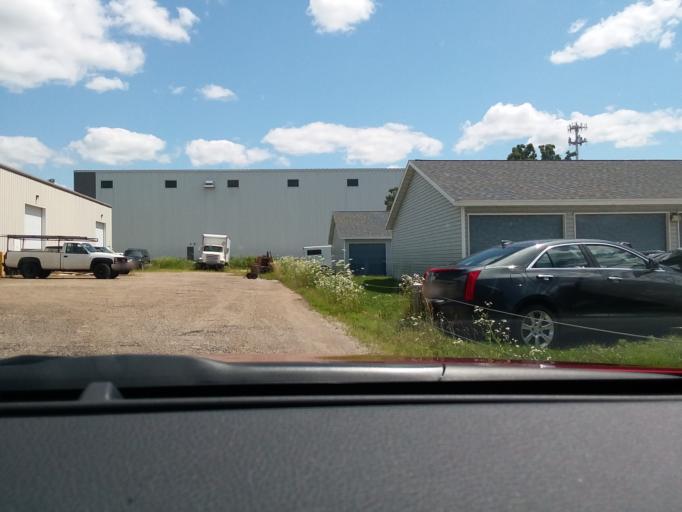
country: US
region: Wisconsin
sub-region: Dane County
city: Windsor
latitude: 43.2023
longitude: -89.3424
